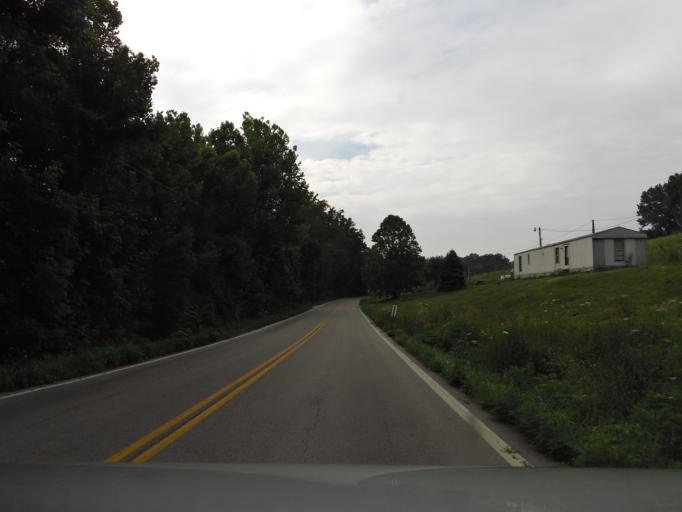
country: US
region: Kentucky
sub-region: Robertson County
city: Mount Olivet
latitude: 38.5155
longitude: -84.1580
